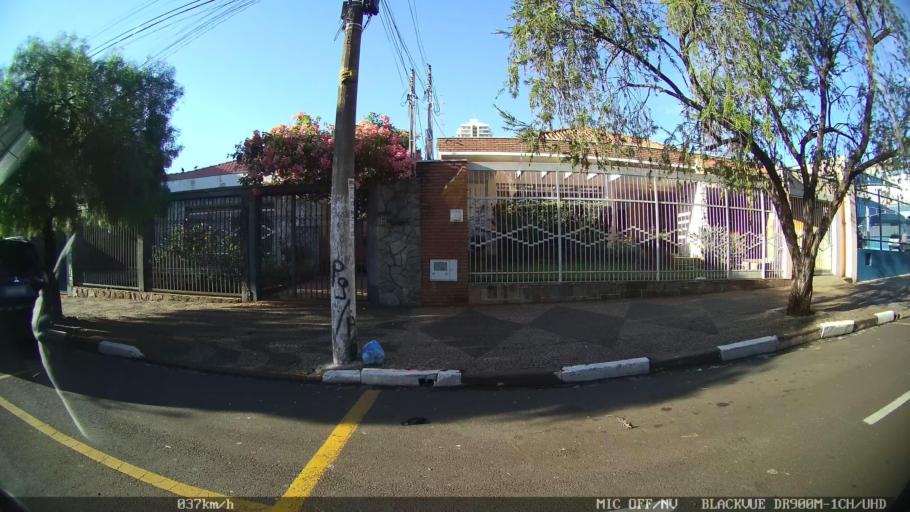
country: BR
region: Sao Paulo
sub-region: Franca
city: Franca
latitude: -20.5311
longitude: -47.3981
